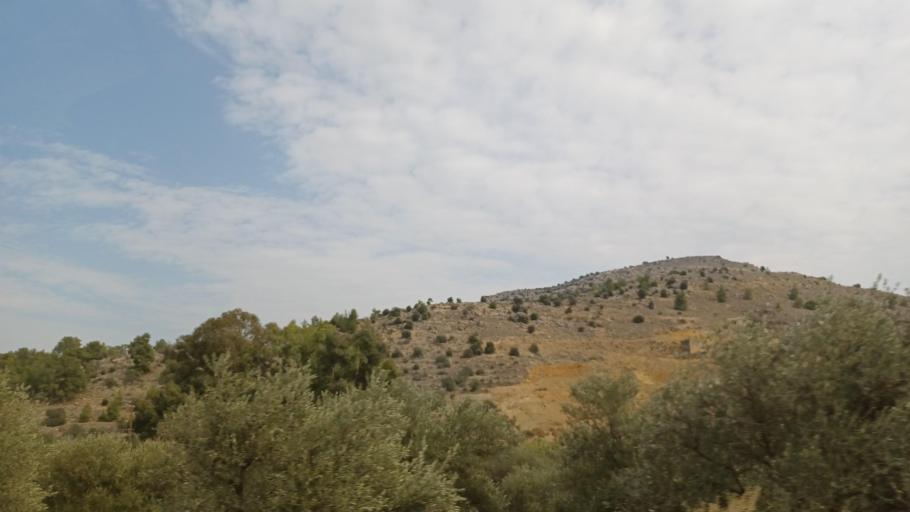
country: CY
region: Lefkosia
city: Klirou
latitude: 35.0483
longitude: 33.1248
